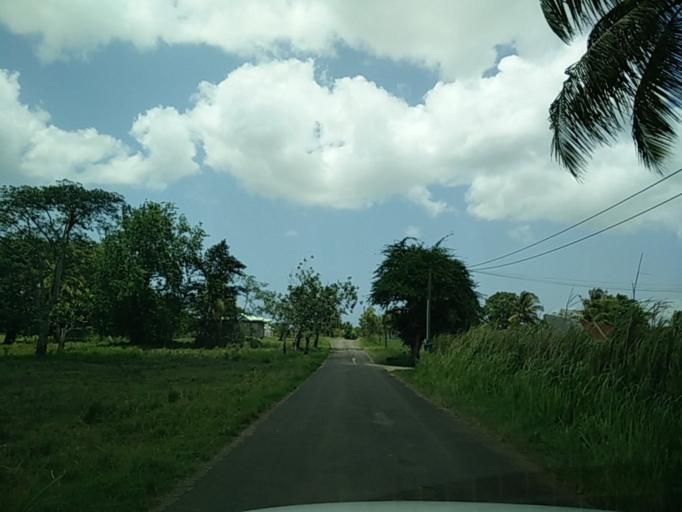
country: GP
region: Guadeloupe
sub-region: Guadeloupe
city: Les Abymes
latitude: 16.2865
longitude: -61.5229
